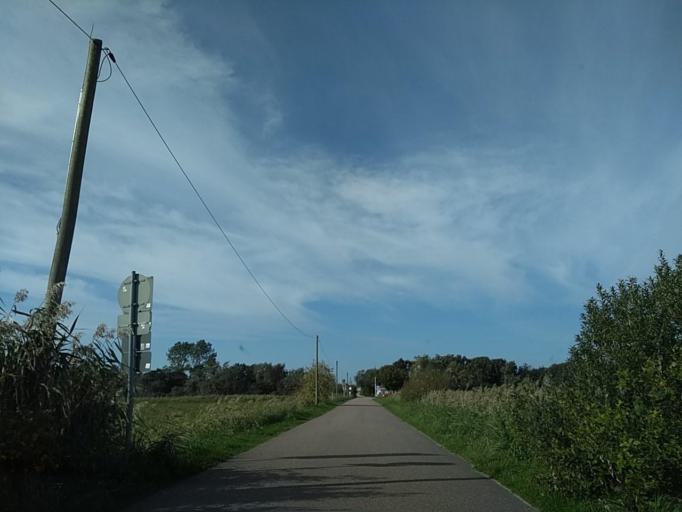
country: DE
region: Mecklenburg-Vorpommern
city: Seeheilbad Graal-Muritz
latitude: 54.2603
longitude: 12.2538
